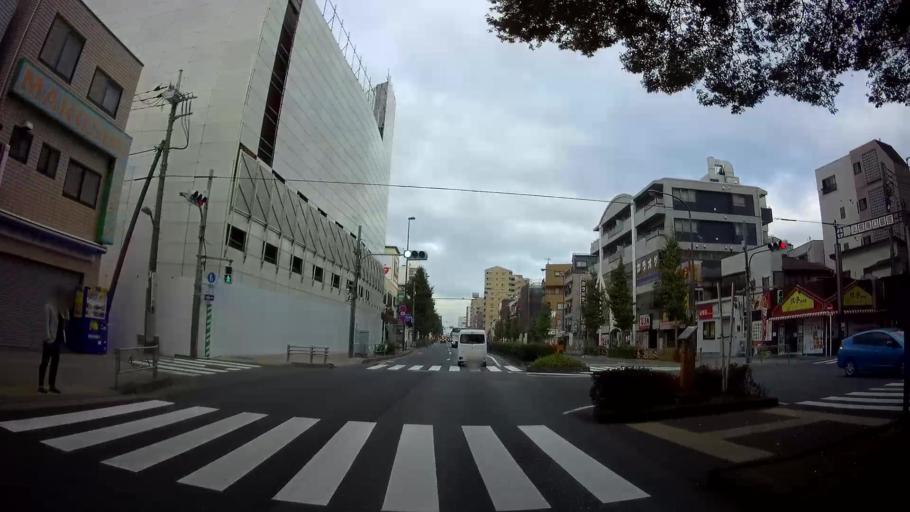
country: JP
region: Saitama
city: Shimotoda
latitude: 35.7610
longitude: 139.6750
